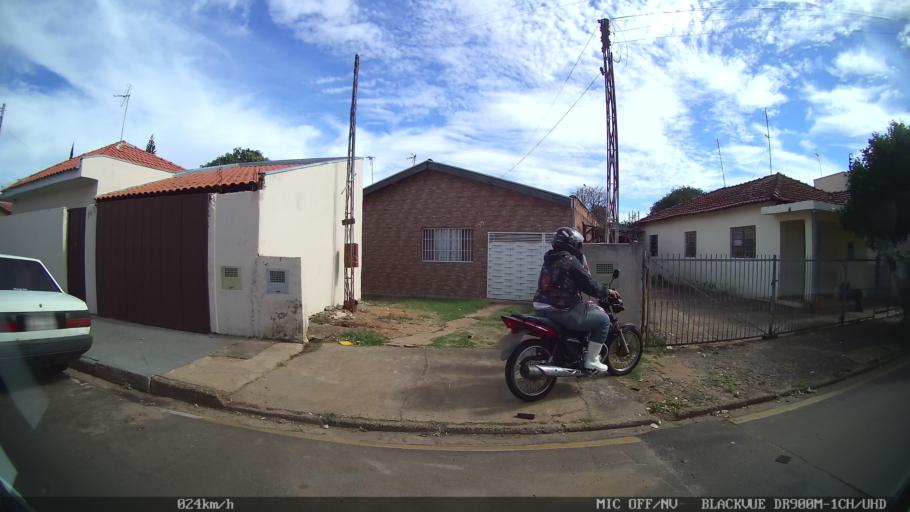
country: BR
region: Sao Paulo
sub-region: Catanduva
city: Catanduva
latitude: -21.1326
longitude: -48.9576
